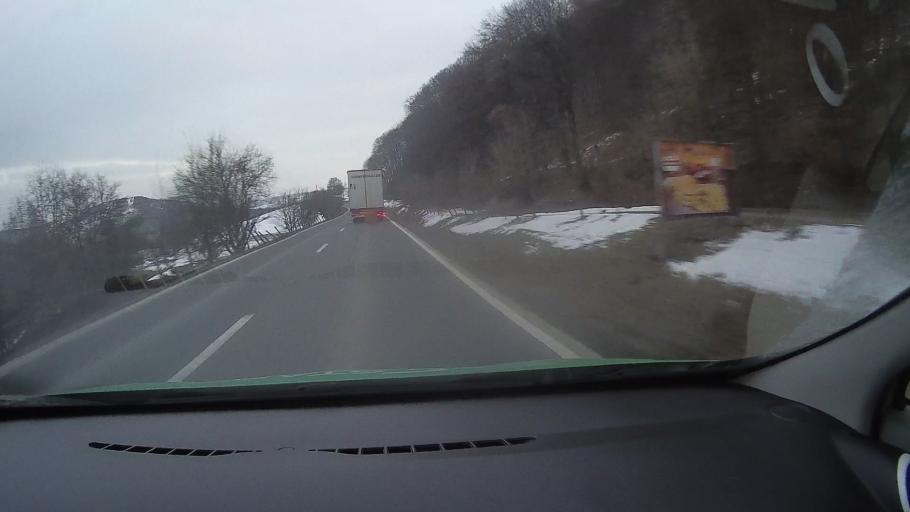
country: RO
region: Harghita
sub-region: Municipiul Odorheiu Secuiesc
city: Odorheiu Secuiesc
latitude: 46.3296
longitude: 25.2753
